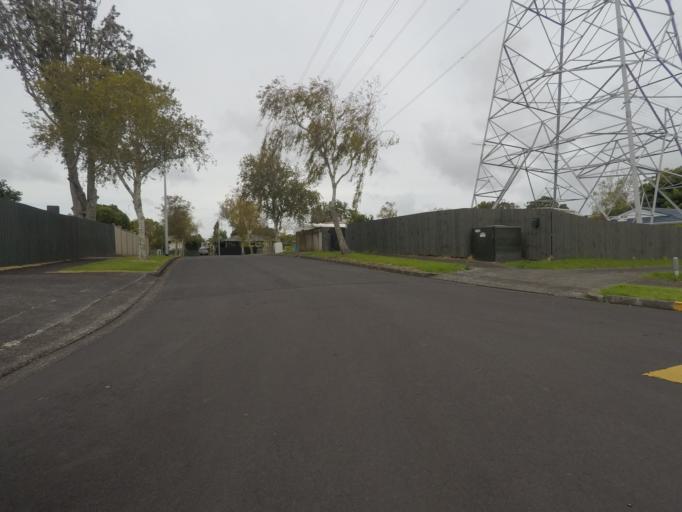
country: NZ
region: Auckland
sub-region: Auckland
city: Rosebank
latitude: -36.8929
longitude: 174.6766
